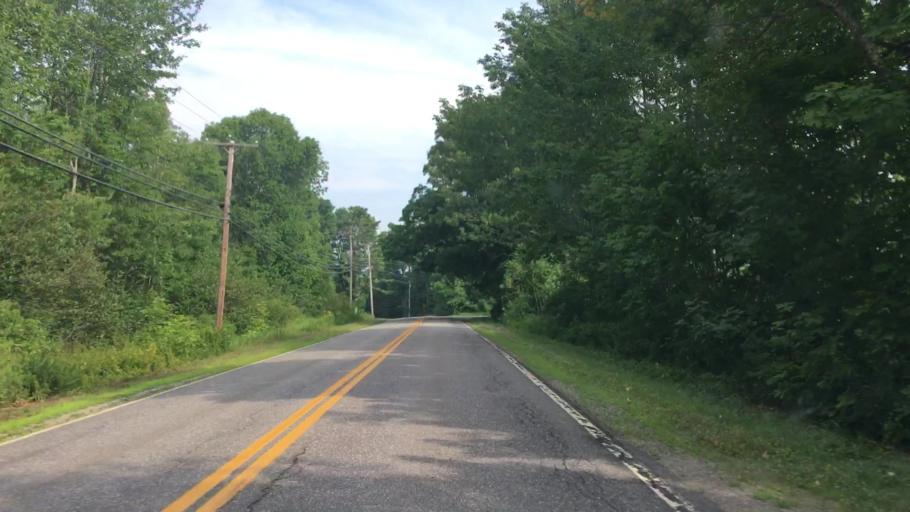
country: US
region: Maine
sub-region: Lincoln County
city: Waldoboro
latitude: 44.0710
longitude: -69.3630
